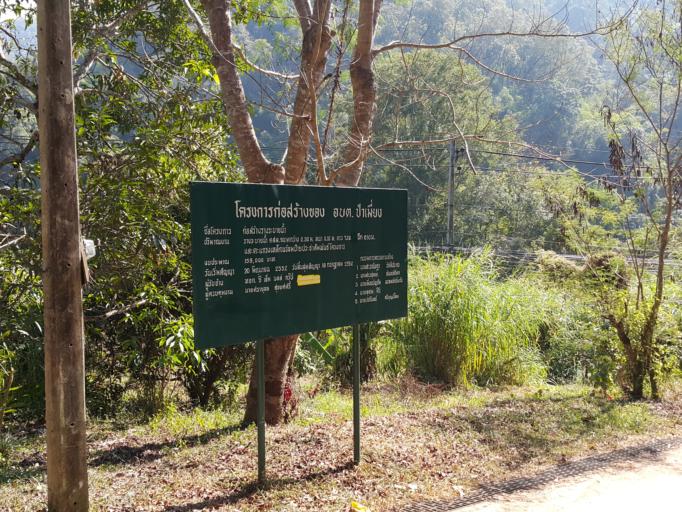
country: TH
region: Chiang Mai
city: Mae On
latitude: 19.0024
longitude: 99.2883
